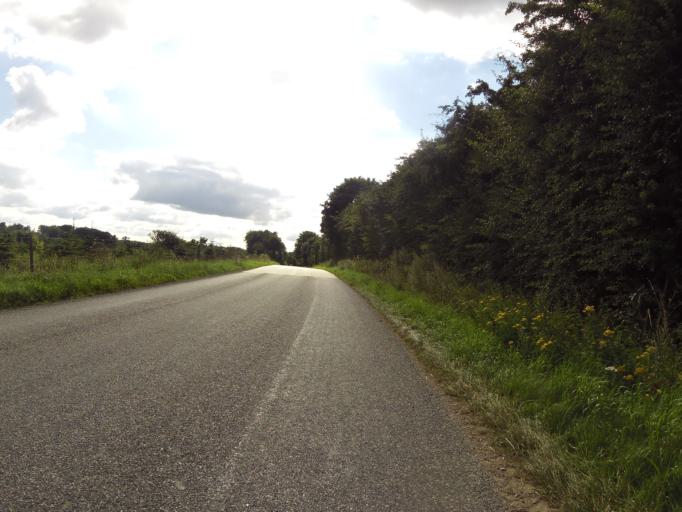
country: DK
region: South Denmark
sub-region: Haderslev Kommune
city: Haderslev
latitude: 55.2067
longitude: 9.4268
